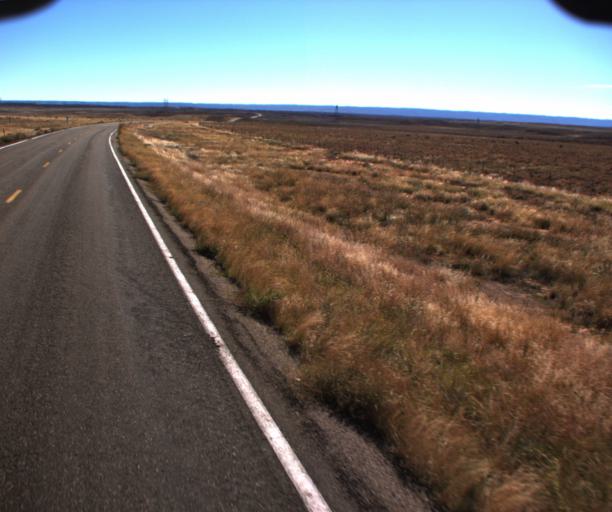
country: US
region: Arizona
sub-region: Coconino County
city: Fredonia
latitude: 36.9217
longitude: -112.4418
